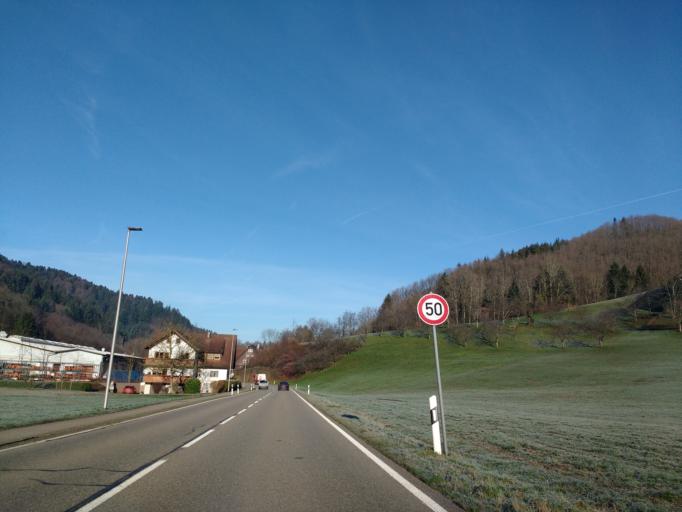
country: DE
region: Baden-Wuerttemberg
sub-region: Freiburg Region
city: Oppenau
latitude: 48.4346
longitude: 8.1744
